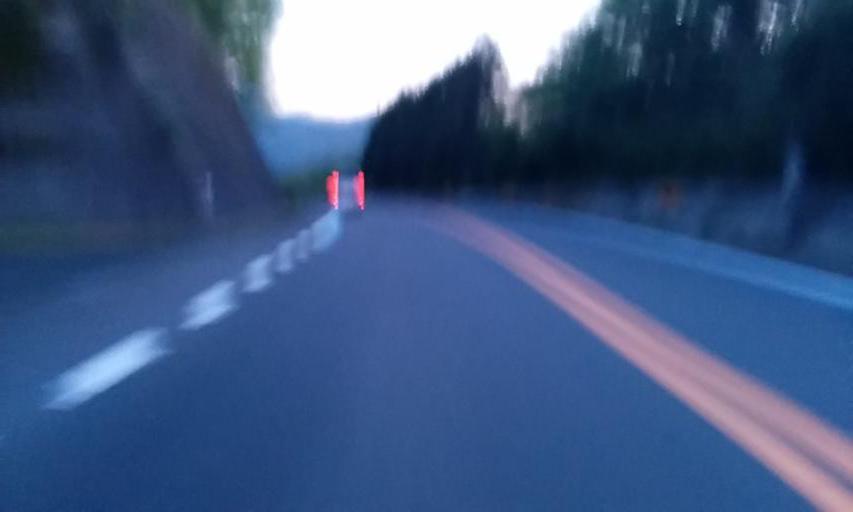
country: JP
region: Ehime
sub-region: Nishiuwa-gun
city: Ikata-cho
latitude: 33.5466
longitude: 132.4211
